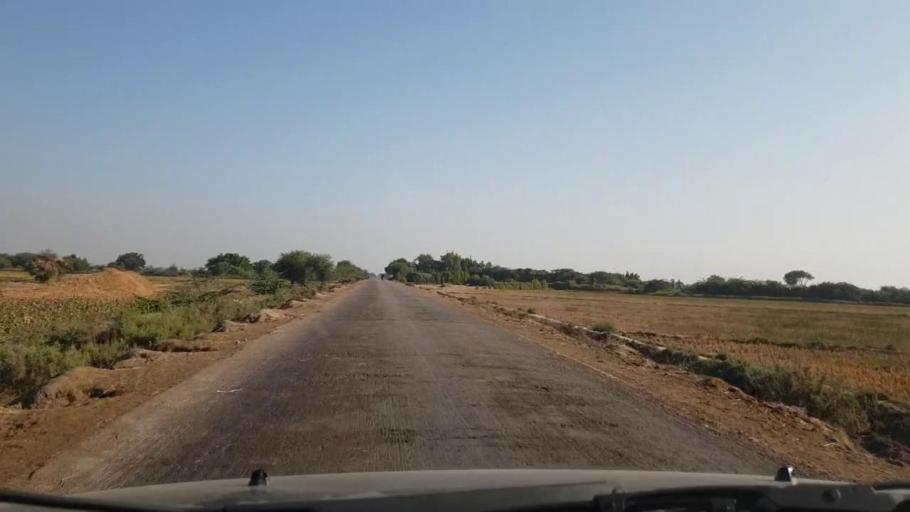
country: PK
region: Sindh
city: Tando Bago
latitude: 24.8595
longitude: 69.0453
